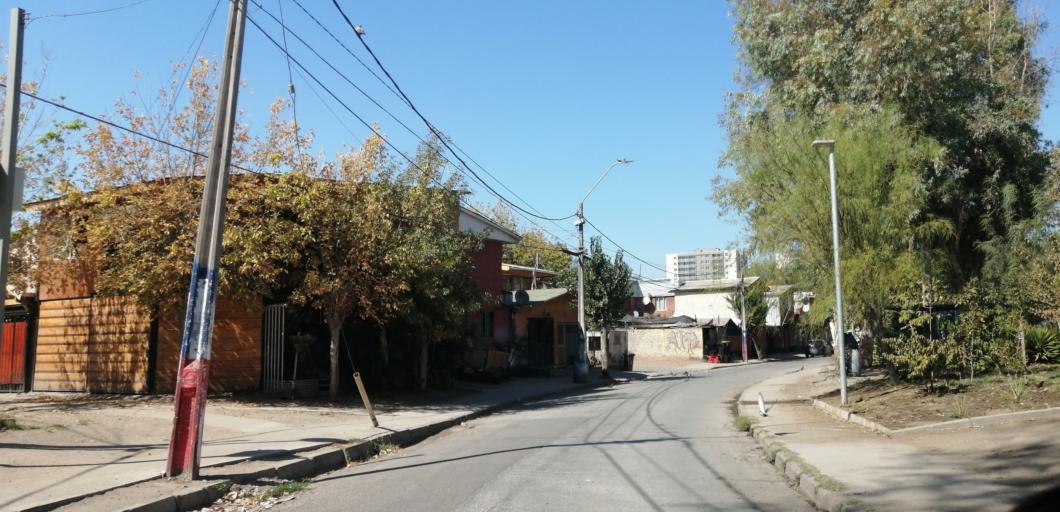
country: CL
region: Santiago Metropolitan
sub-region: Provincia de Santiago
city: Lo Prado
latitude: -33.4477
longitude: -70.7589
